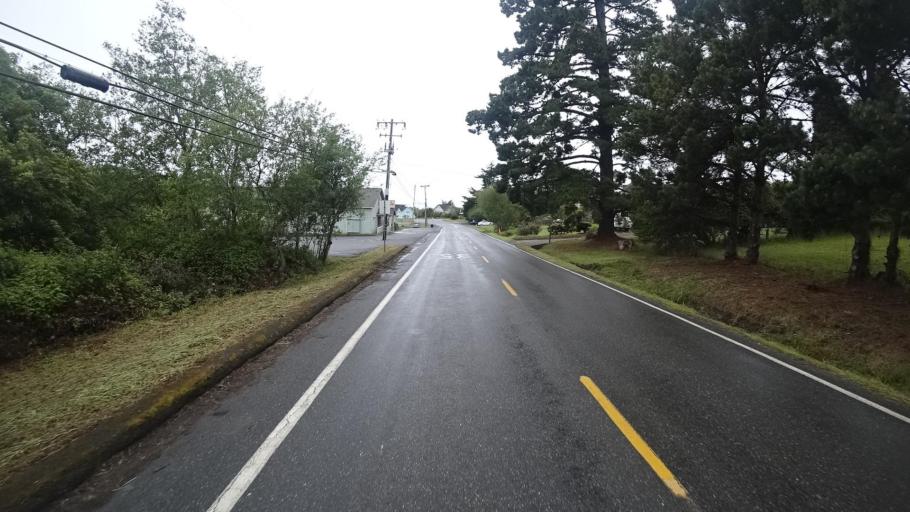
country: US
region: California
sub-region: Humboldt County
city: Bayside
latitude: 40.8418
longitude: -124.0623
